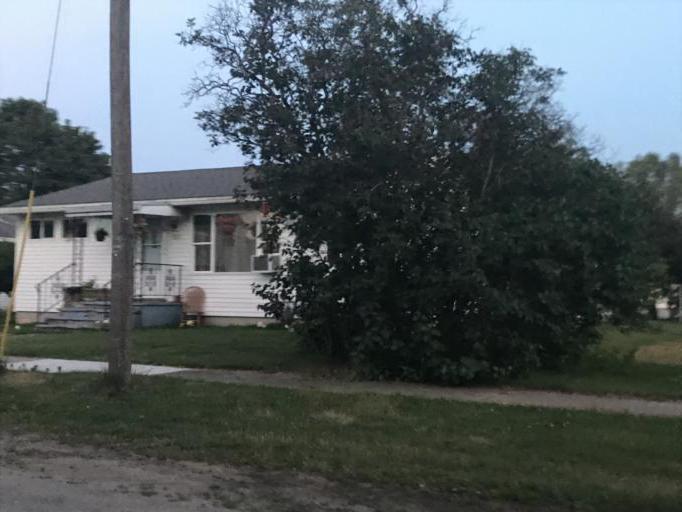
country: US
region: Wisconsin
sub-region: Marinette County
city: Marinette
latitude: 45.0871
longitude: -87.6172
